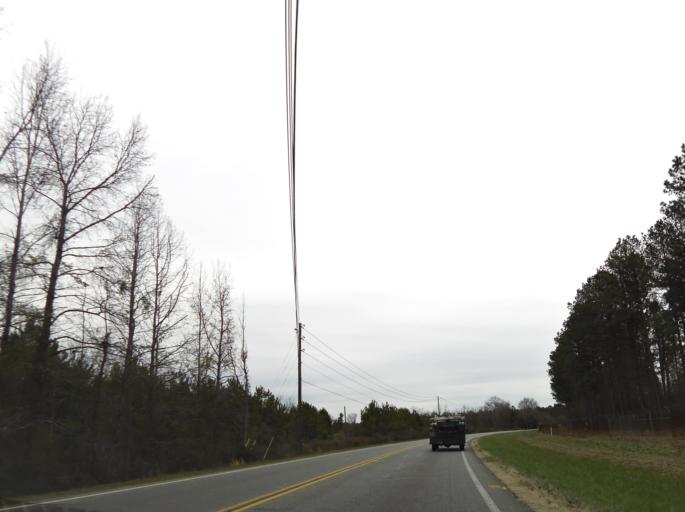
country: US
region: Georgia
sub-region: Peach County
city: Byron
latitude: 32.6714
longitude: -83.7272
